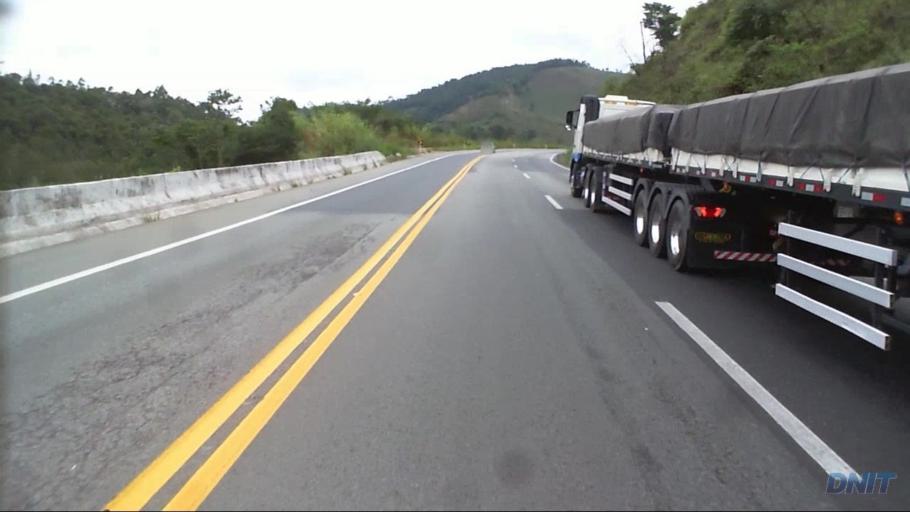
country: BR
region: Minas Gerais
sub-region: Nova Era
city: Nova Era
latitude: -19.6332
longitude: -42.8887
